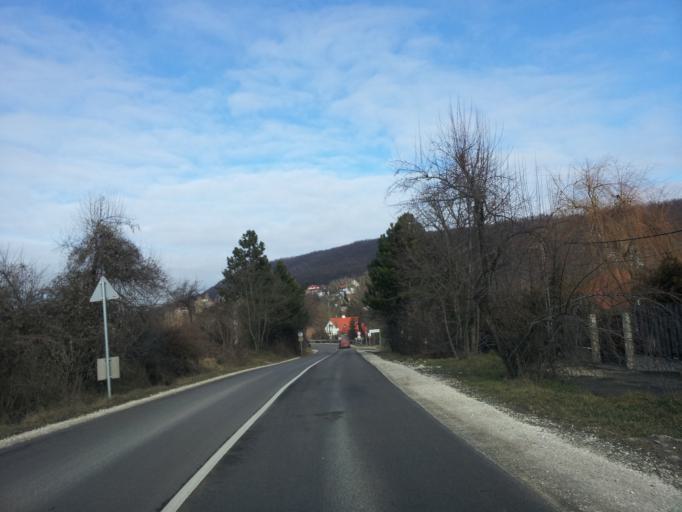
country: HU
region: Pest
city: Solymar
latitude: 47.5551
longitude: 18.9268
